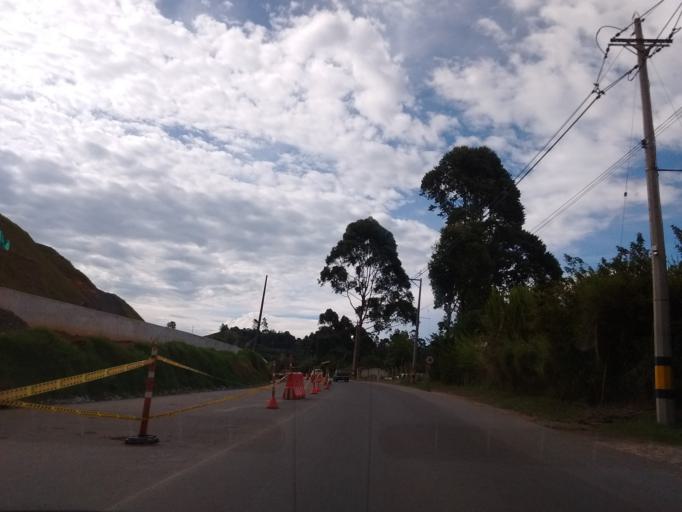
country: CO
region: Antioquia
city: Marinilla
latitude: 6.1643
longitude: -75.3195
